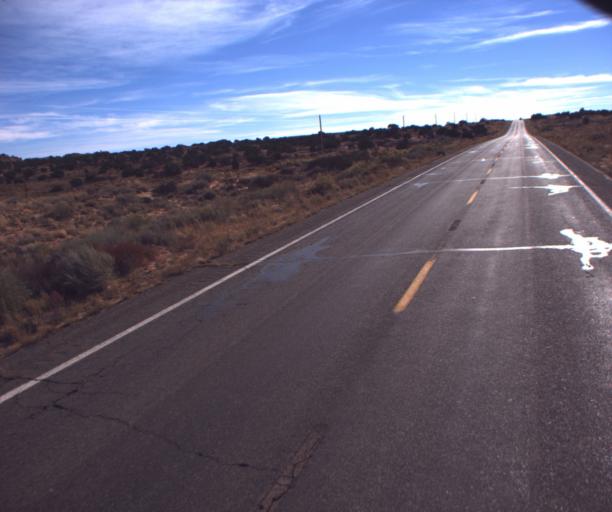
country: US
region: Arizona
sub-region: Coconino County
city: Kaibito
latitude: 36.6018
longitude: -111.1726
